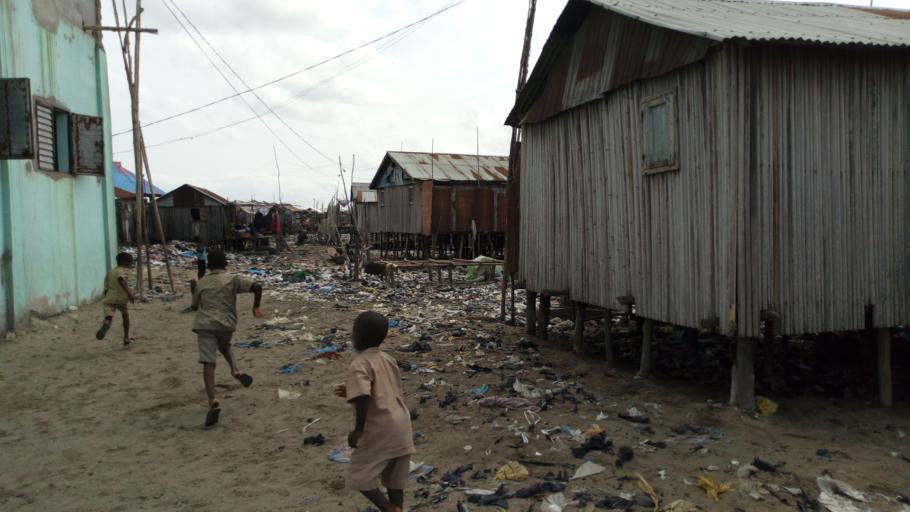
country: BJ
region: Littoral
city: Cotonou
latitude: 6.3905
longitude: 2.4324
